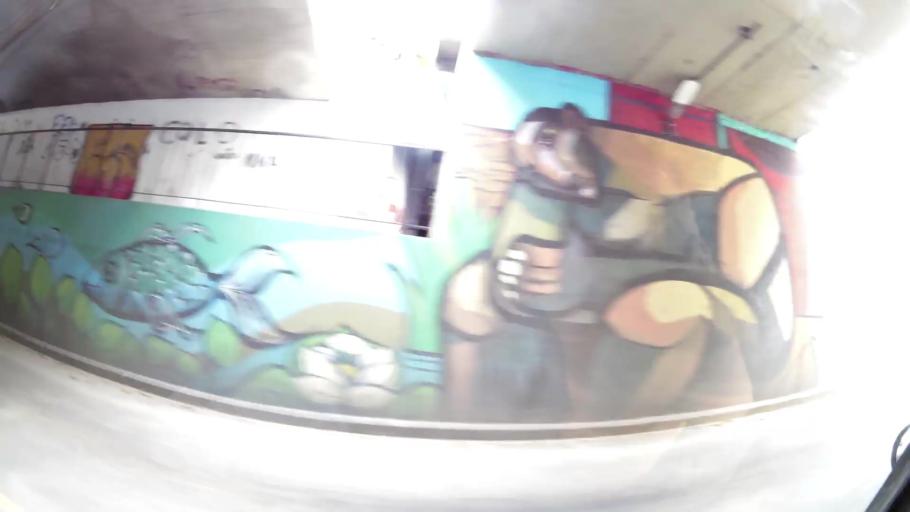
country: AR
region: Buenos Aires
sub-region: Partido de Quilmes
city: Quilmes
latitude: -34.7309
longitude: -58.2562
